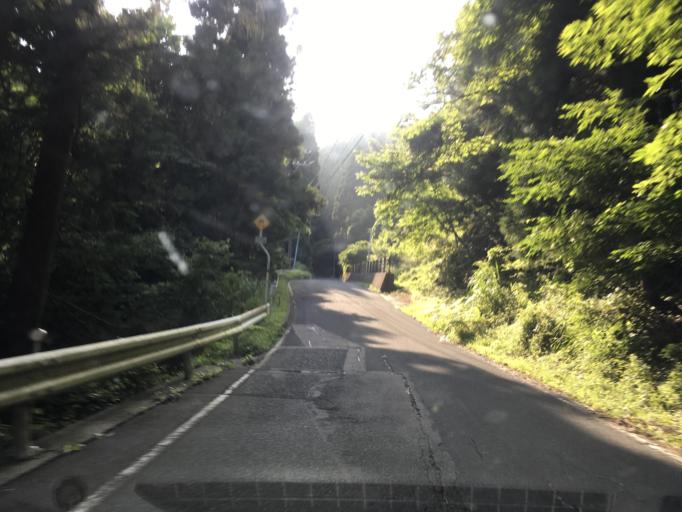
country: JP
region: Iwate
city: Ofunato
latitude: 38.9158
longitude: 141.6142
